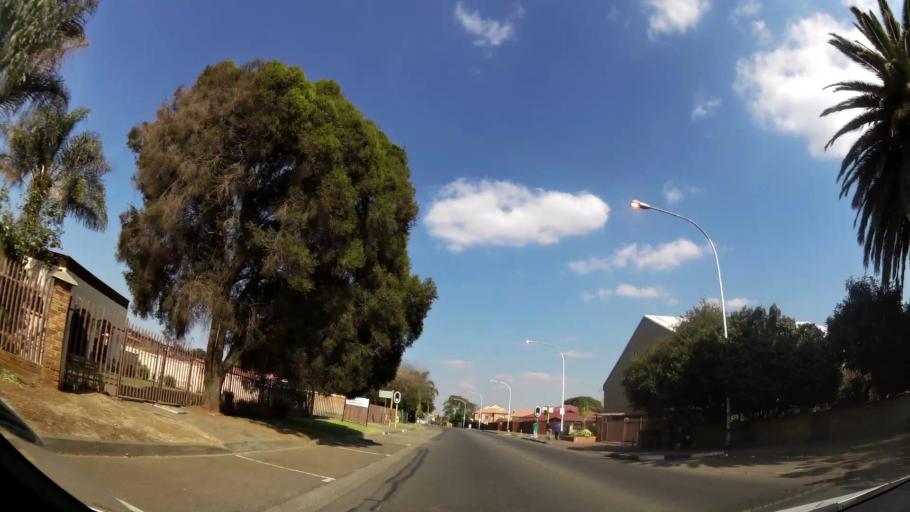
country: ZA
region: Gauteng
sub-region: Ekurhuleni Metropolitan Municipality
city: Boksburg
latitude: -26.1824
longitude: 28.2077
